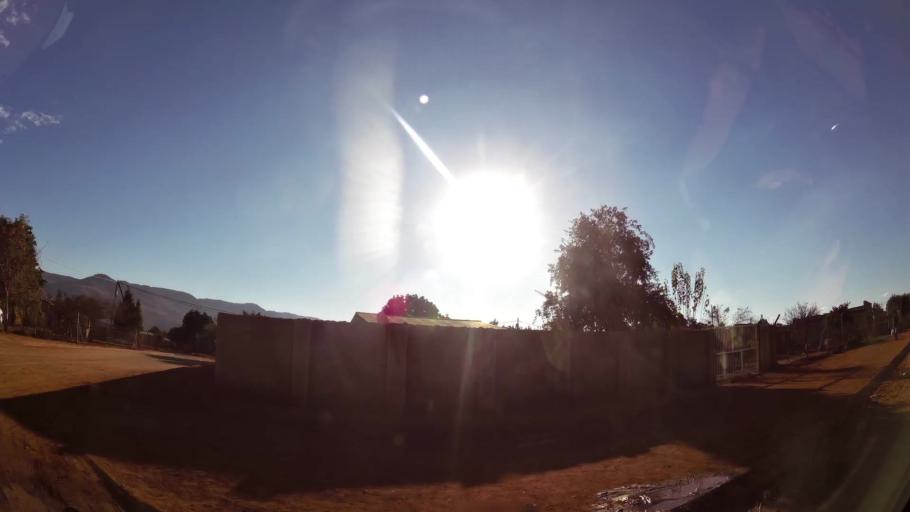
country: ZA
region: Limpopo
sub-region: Waterberg District Municipality
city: Mokopane
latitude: -24.1830
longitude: 28.9829
